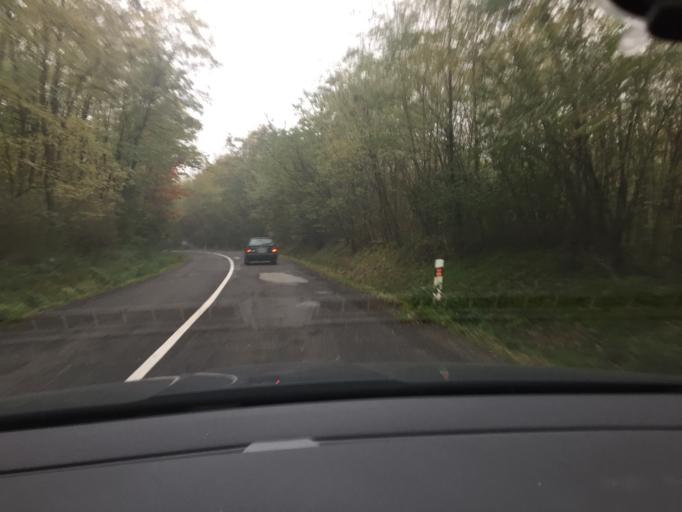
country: SK
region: Banskobystricky
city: Dudince
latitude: 48.1572
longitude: 18.9273
